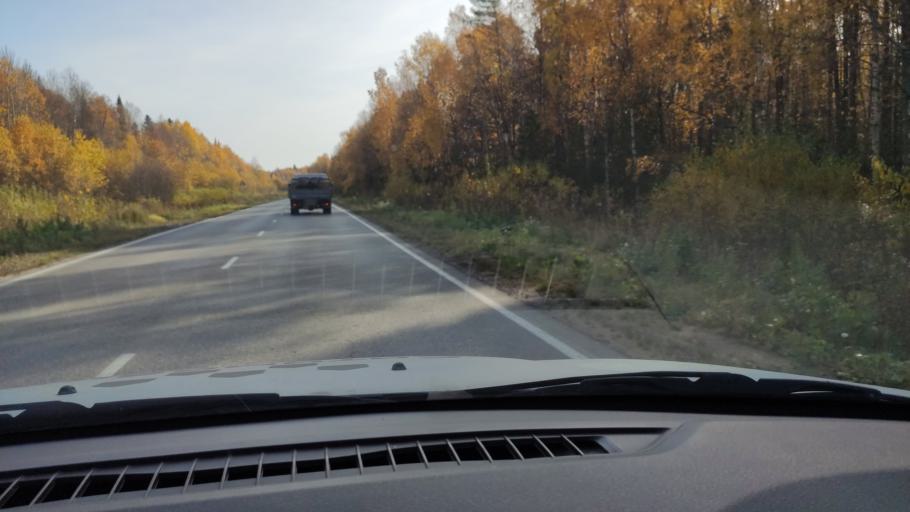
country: RU
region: Perm
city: Novyye Lyady
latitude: 58.0231
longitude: 56.6407
